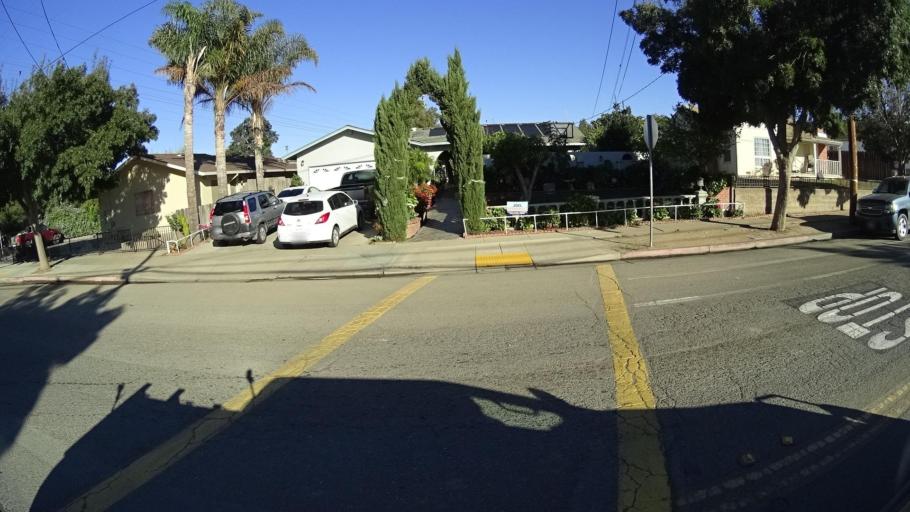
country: US
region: California
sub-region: Monterey County
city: Gonzales
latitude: 36.5104
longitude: -121.4416
